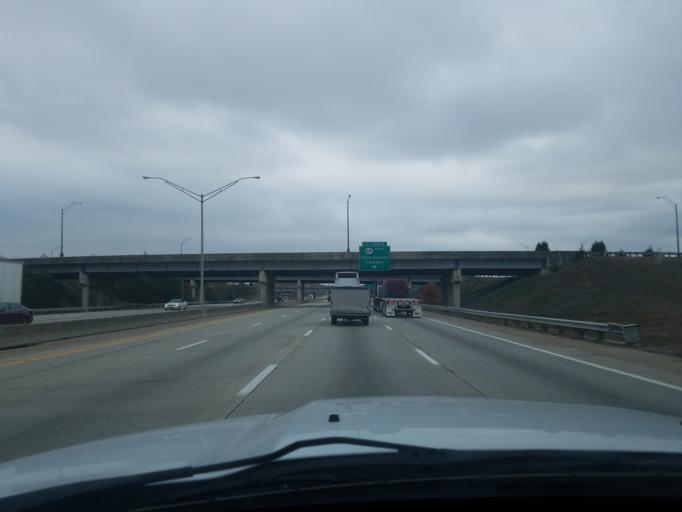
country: US
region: Kentucky
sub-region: Jefferson County
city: Heritage Creek
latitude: 38.1114
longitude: -85.7014
